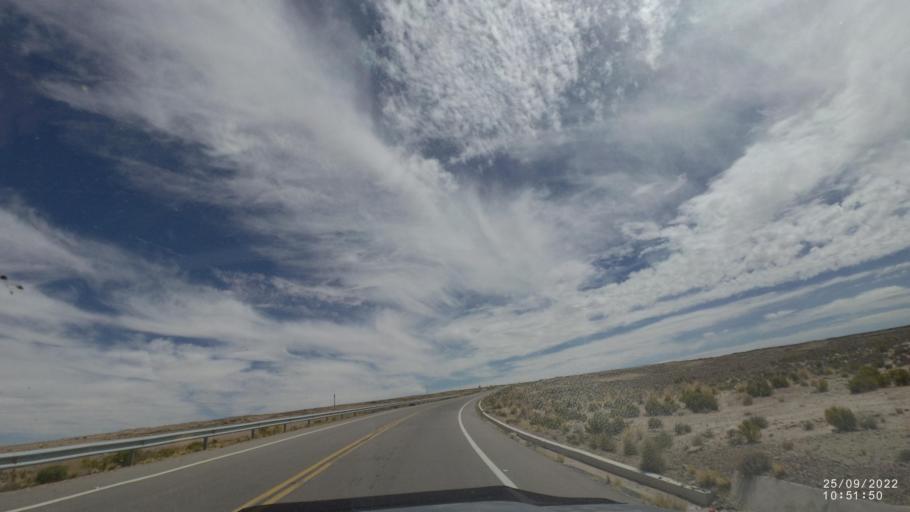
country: BO
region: Oruro
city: Challapata
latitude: -19.5572
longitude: -66.8526
